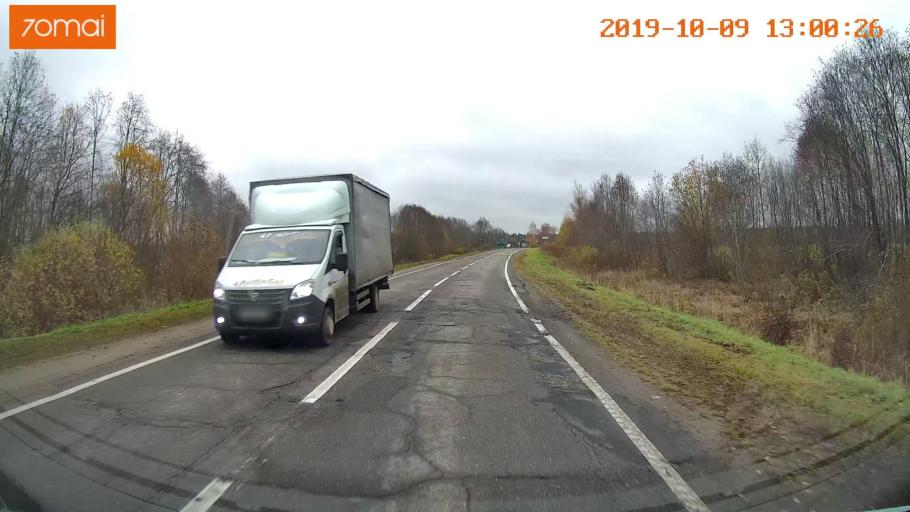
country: RU
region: Jaroslavl
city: Prechistoye
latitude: 58.3773
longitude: 40.4803
